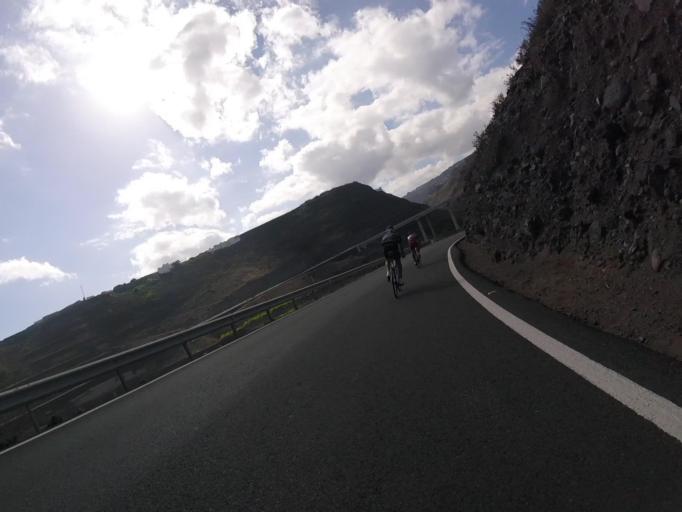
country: ES
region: Canary Islands
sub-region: Provincia de Las Palmas
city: Moya
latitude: 28.1421
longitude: -15.5900
